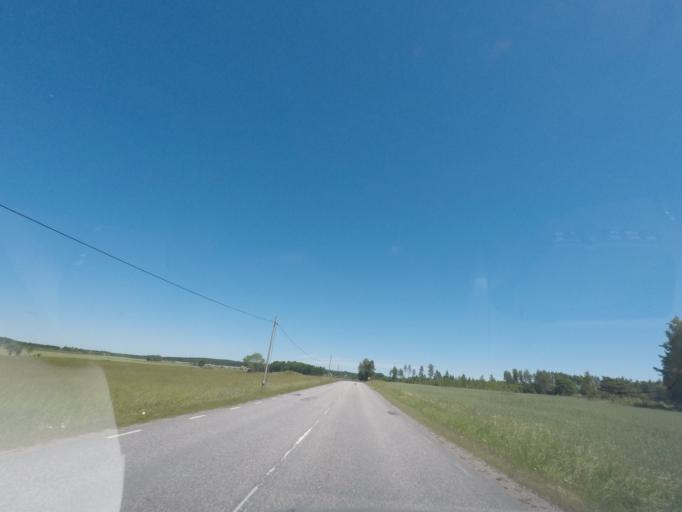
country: SE
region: Vaestmanland
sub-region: Vasteras
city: Tillberga
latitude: 59.6610
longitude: 16.7000
